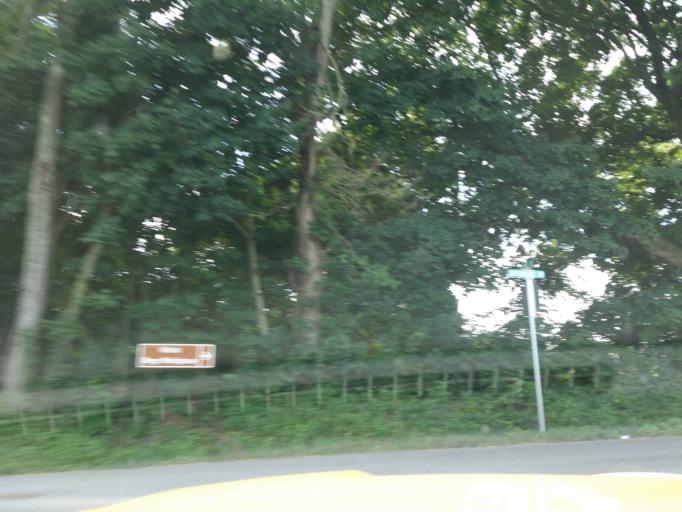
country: US
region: Pennsylvania
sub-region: Lebanon County
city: Jonestown
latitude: 40.4193
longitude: -76.4729
